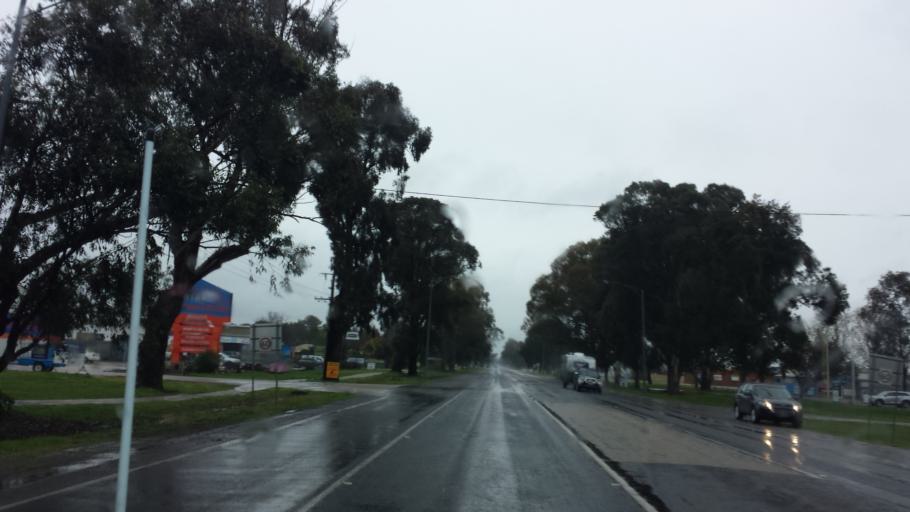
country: AU
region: Victoria
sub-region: Benalla
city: Benalla
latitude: -36.5469
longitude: 146.0012
